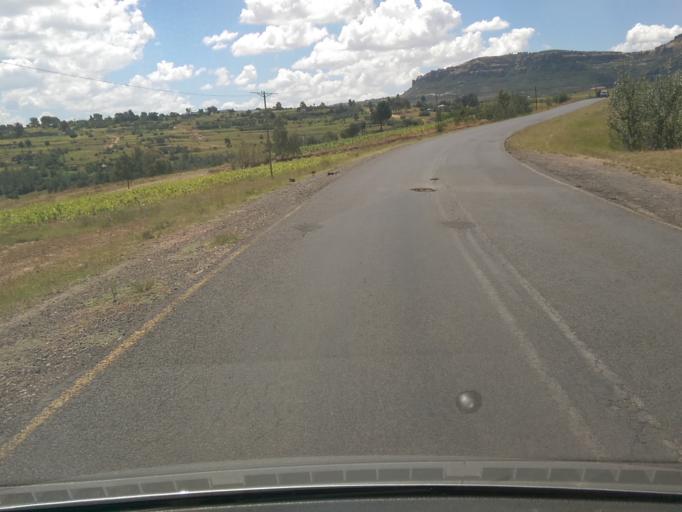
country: LS
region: Maseru
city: Nako
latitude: -29.4327
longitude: 27.6756
